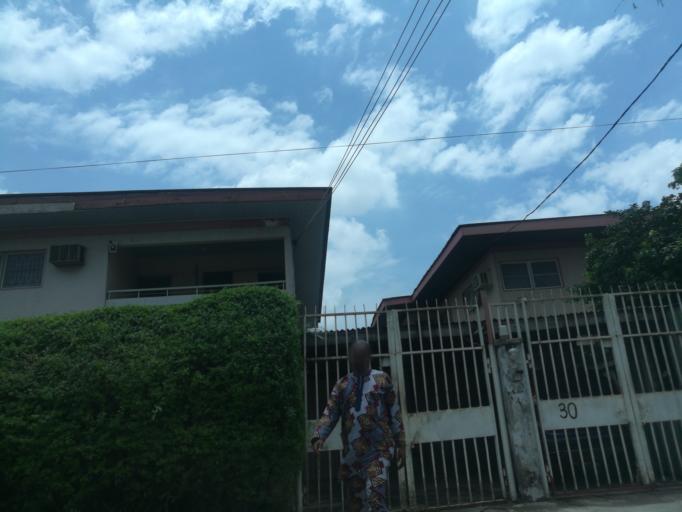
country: NG
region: Lagos
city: Somolu
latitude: 6.5487
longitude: 3.3609
